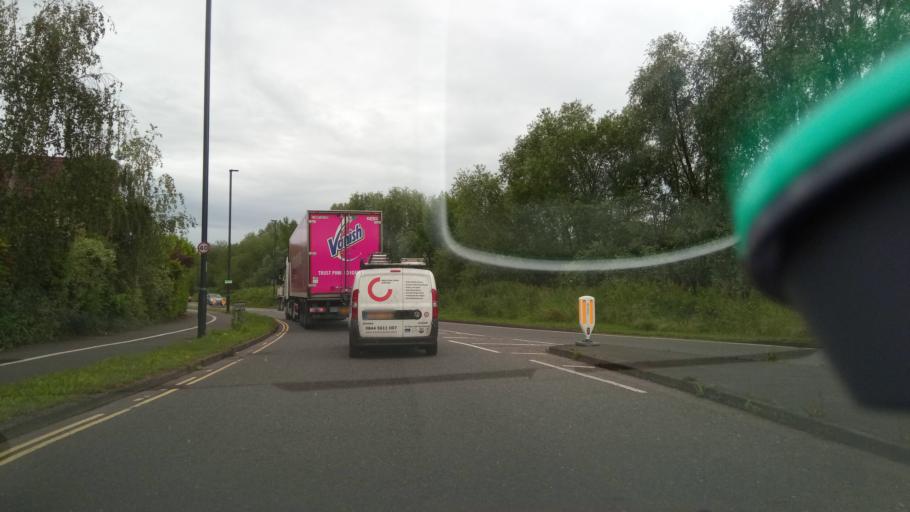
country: GB
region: England
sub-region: Derbyshire
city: Melbourne
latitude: 52.8669
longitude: -1.4487
